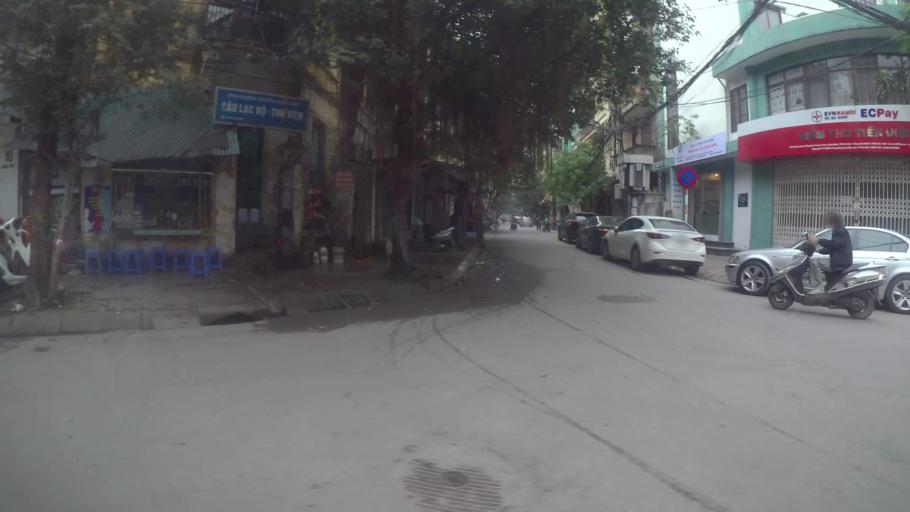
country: VN
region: Ha Noi
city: Hoan Kiem
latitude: 21.0434
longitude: 105.8456
